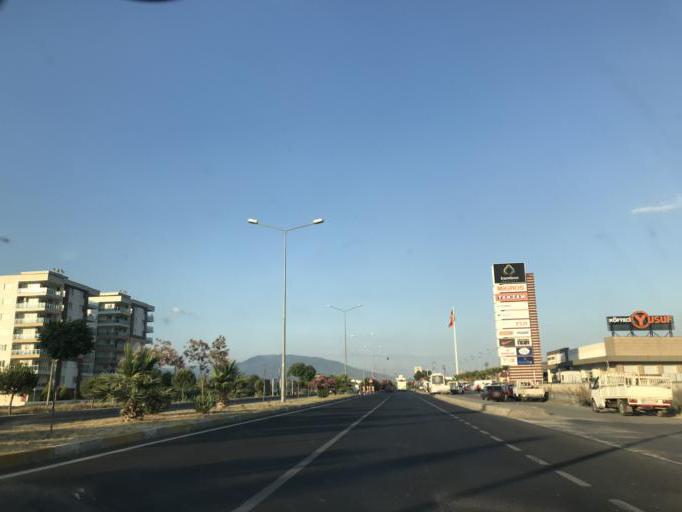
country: TR
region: Aydin
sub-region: Nazilli
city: Isabeyli
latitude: 37.8990
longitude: 28.2761
